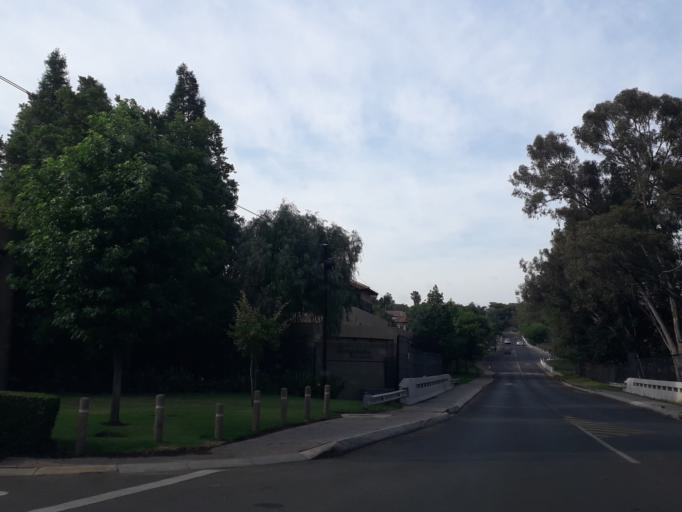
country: ZA
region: Gauteng
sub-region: City of Johannesburg Metropolitan Municipality
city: Johannesburg
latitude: -26.0864
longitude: 28.0392
